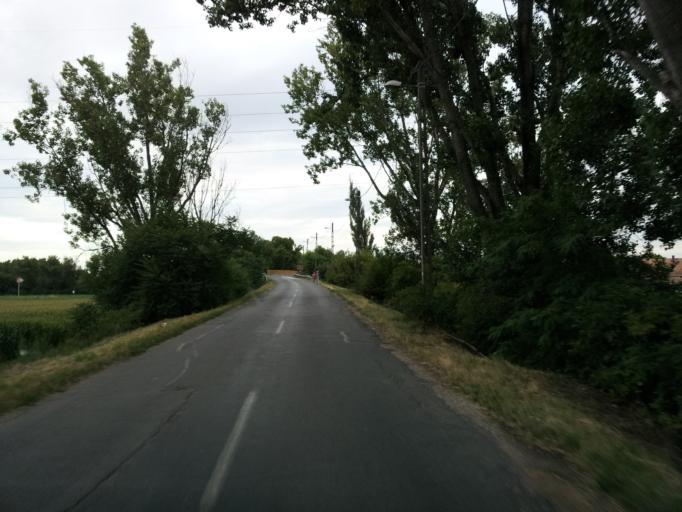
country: HU
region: Somogy
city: Balatonszabadi
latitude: 46.8841
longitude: 18.1413
